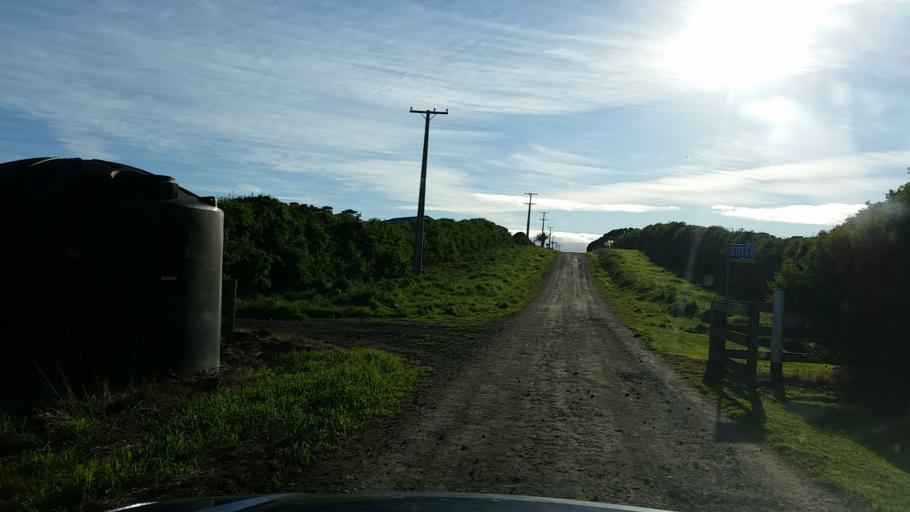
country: NZ
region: Taranaki
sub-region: South Taranaki District
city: Patea
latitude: -39.7161
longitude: 174.4272
